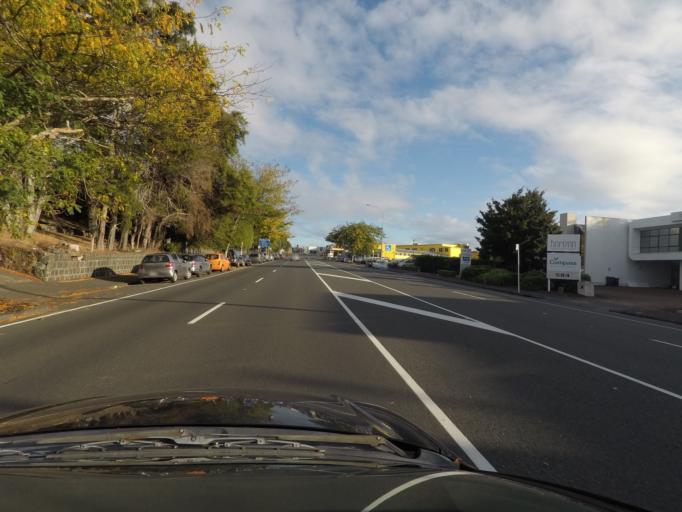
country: NZ
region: Auckland
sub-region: Auckland
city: Auckland
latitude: -36.8963
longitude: 174.8011
